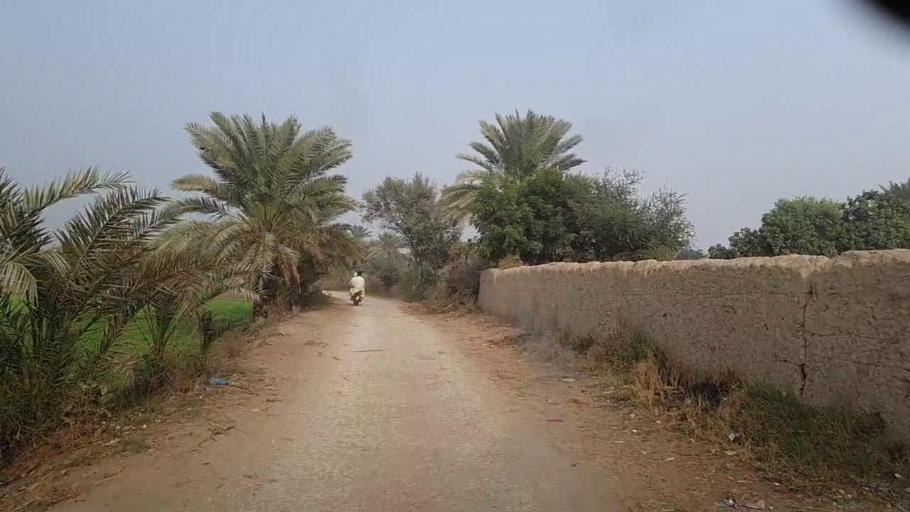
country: PK
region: Sindh
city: Bozdar
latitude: 27.1441
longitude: 68.6679
